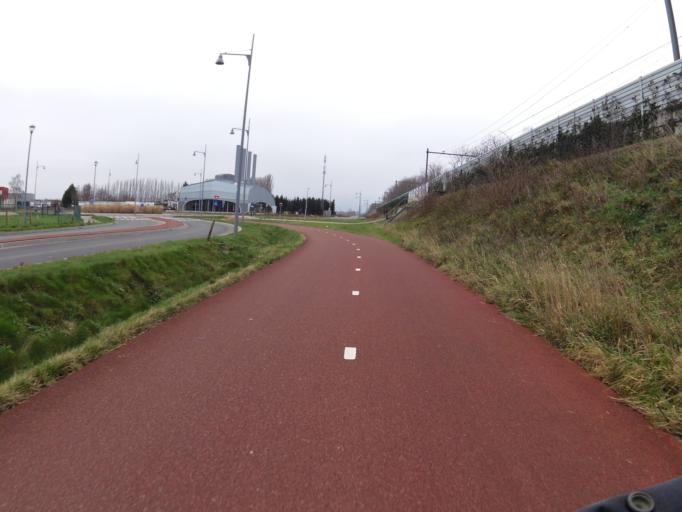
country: NL
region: Gelderland
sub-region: Gemeente Nijmegen
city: Nijmegen
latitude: 51.8683
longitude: 5.8590
